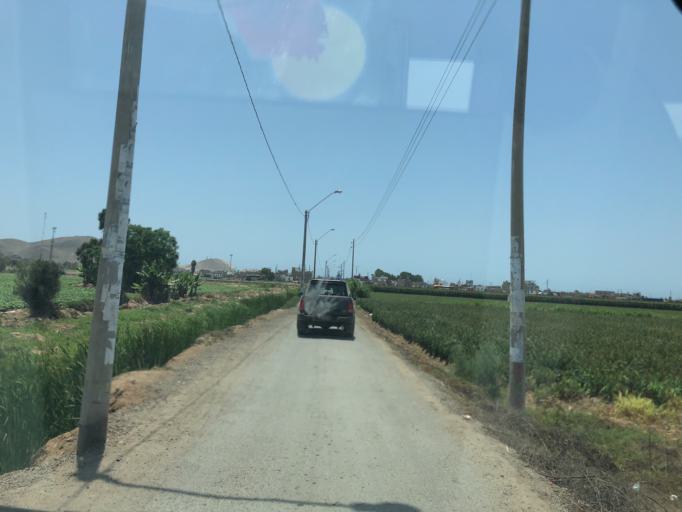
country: PE
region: Lima
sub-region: Provincia de Canete
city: San Vicente de Canete
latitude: -13.0231
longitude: -76.4717
